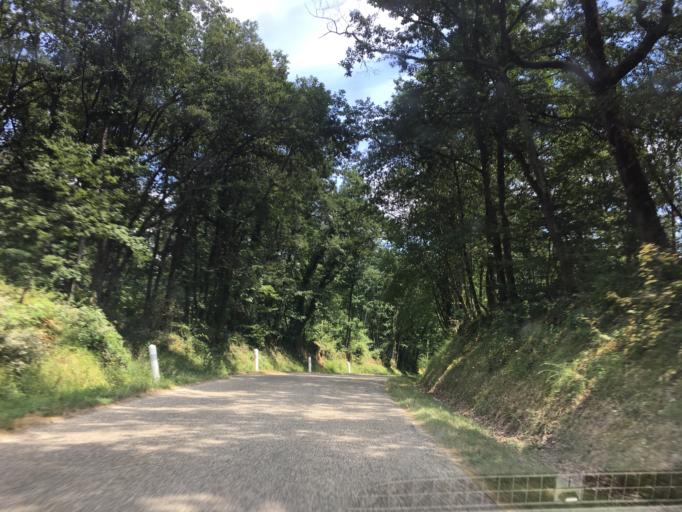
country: FR
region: Midi-Pyrenees
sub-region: Departement du Gers
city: Fleurance
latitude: 43.8165
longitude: 0.5797
